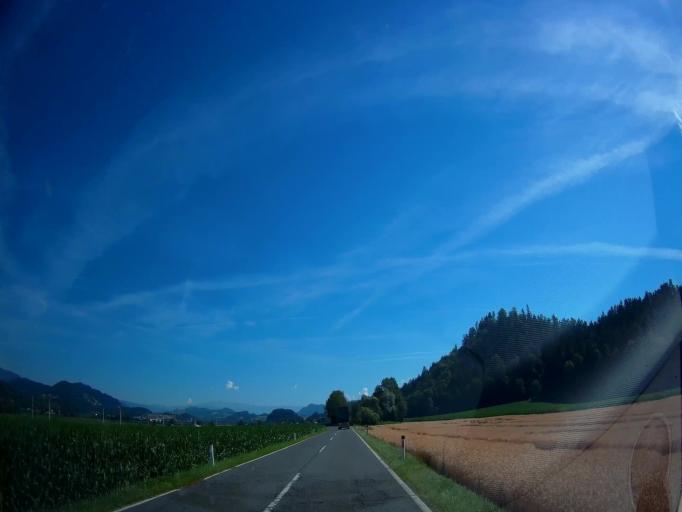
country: AT
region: Carinthia
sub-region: Politischer Bezirk Klagenfurt Land
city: Maria Saal
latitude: 46.7080
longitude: 14.3662
